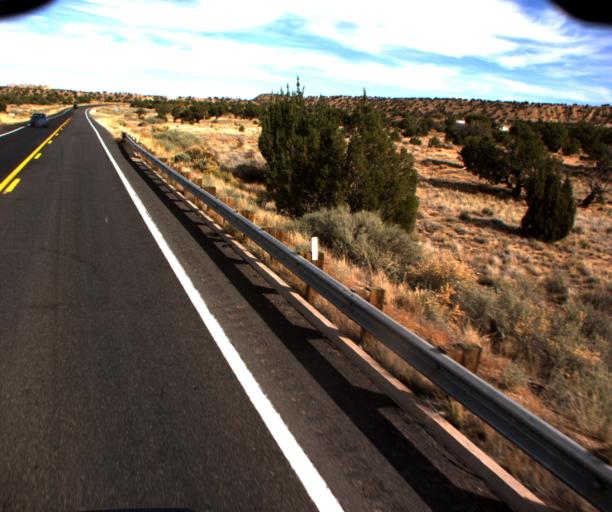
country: US
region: Arizona
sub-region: Navajo County
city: Kayenta
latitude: 36.6977
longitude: -110.3400
